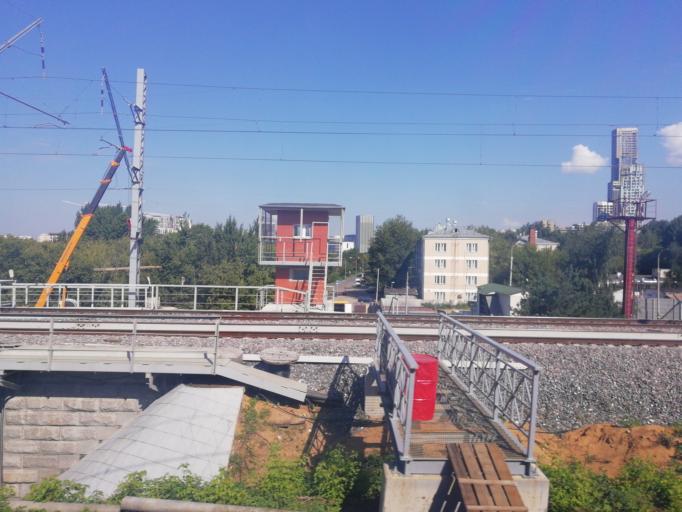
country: RU
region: Moskovskaya
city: Presnenskiy
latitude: 55.7478
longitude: 37.5241
